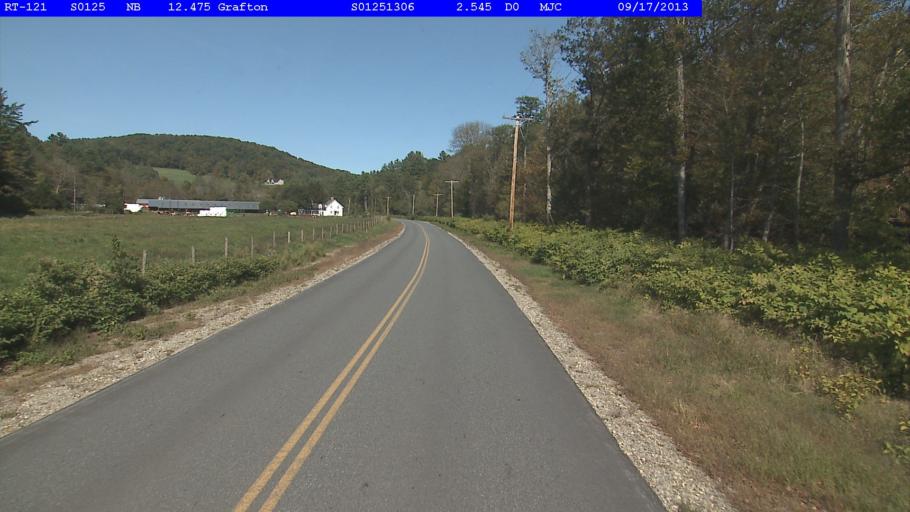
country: US
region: Vermont
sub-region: Windsor County
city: Chester
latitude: 43.1751
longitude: -72.5811
